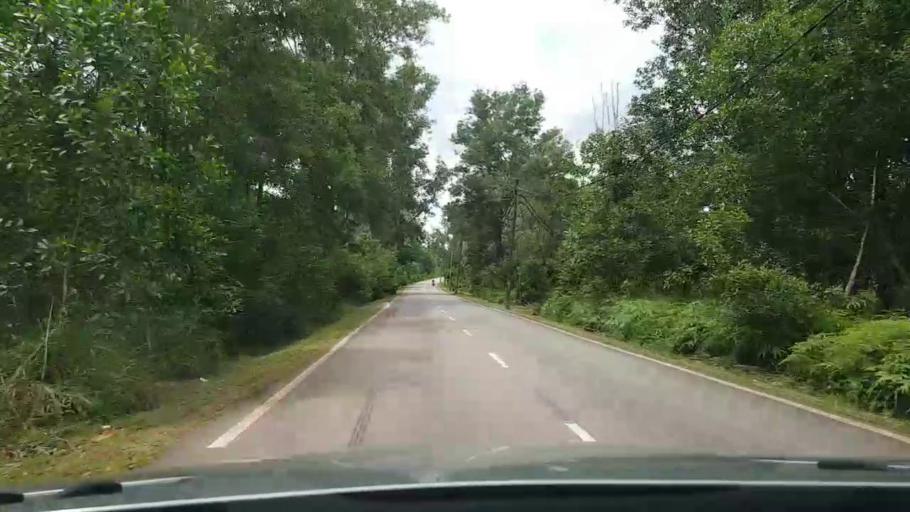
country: MY
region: Pahang
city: Pekan
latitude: 3.1558
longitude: 102.9722
